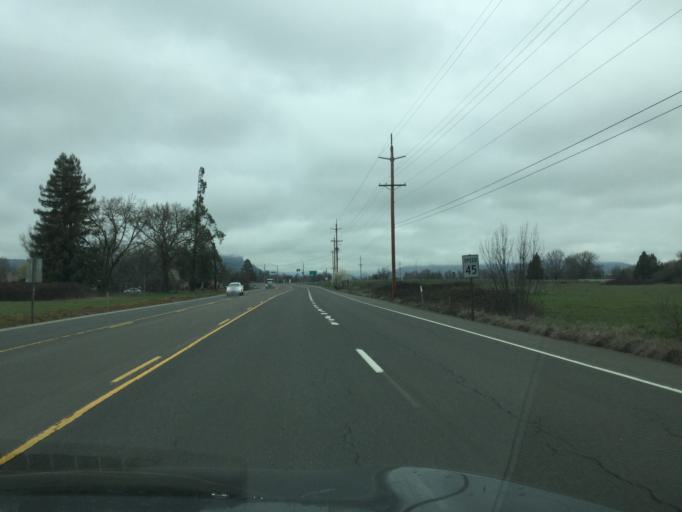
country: US
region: Oregon
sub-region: Jackson County
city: Central Point
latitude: 42.4000
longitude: -122.9408
